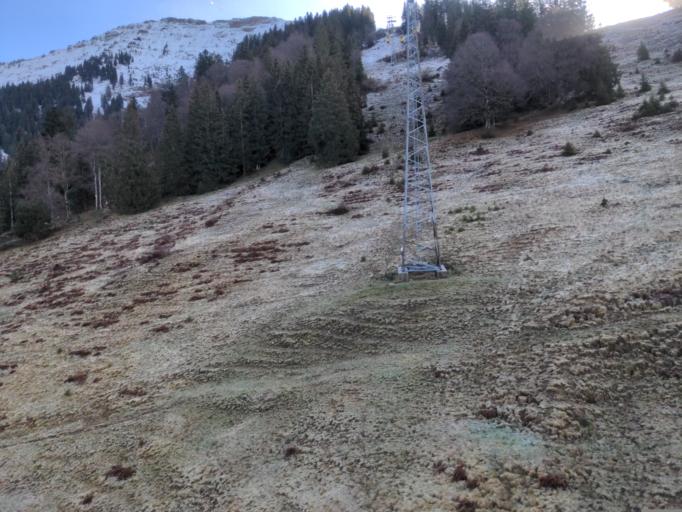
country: DE
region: Bavaria
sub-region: Swabia
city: Balderschwang
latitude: 47.5034
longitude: 10.0632
